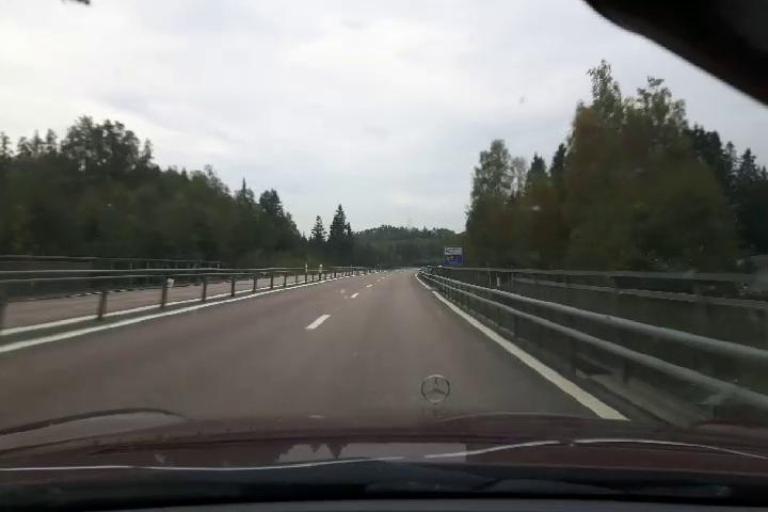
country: SE
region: Vaesternorrland
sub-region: Haernoesands Kommun
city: Haernoesand
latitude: 62.8172
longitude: 17.9686
